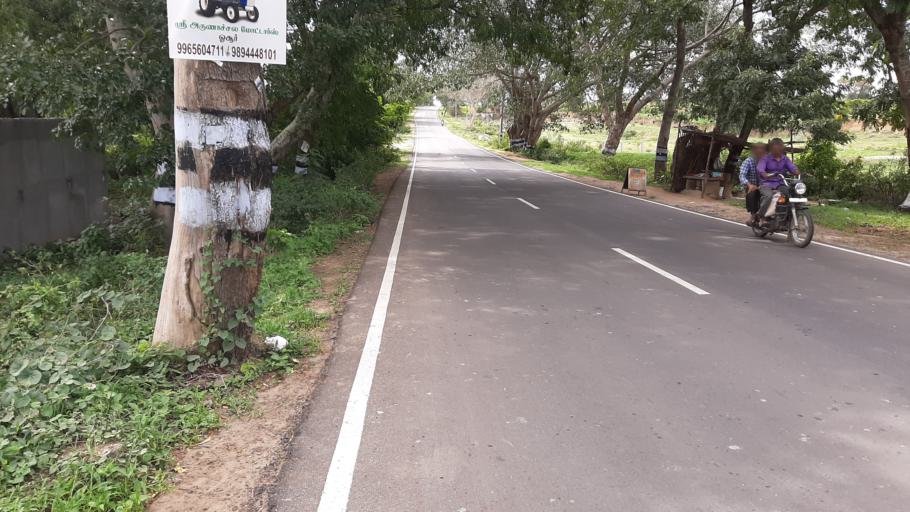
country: IN
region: Tamil Nadu
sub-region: Krishnagiri
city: Denkanikota
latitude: 12.5329
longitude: 77.7786
